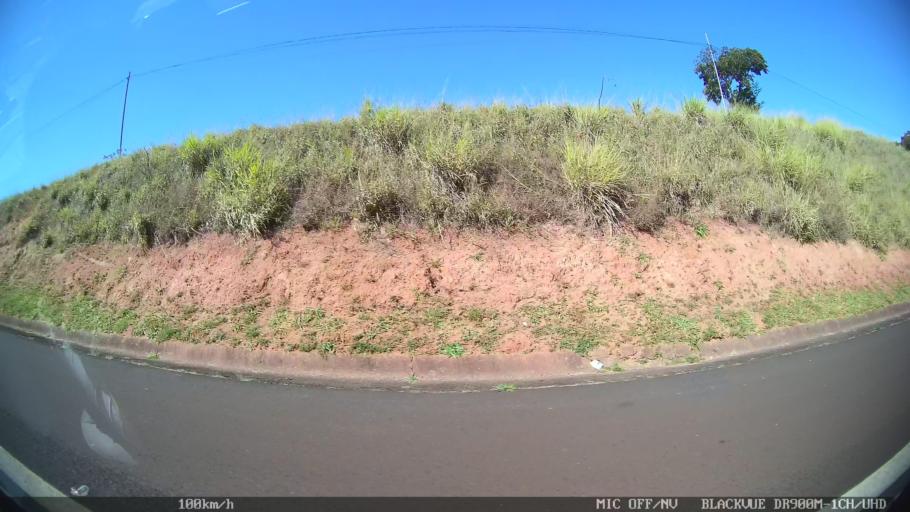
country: BR
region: Sao Paulo
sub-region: Franca
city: Franca
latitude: -20.5660
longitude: -47.4213
